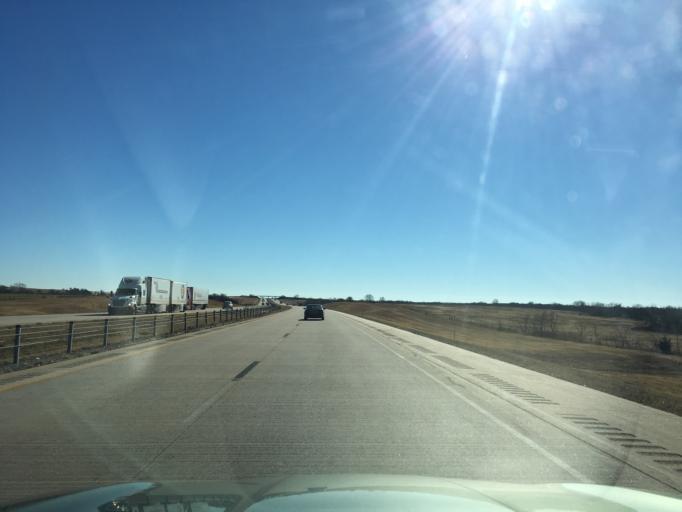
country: US
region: Oklahoma
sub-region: Kay County
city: Tonkawa
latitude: 36.5041
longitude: -97.3358
